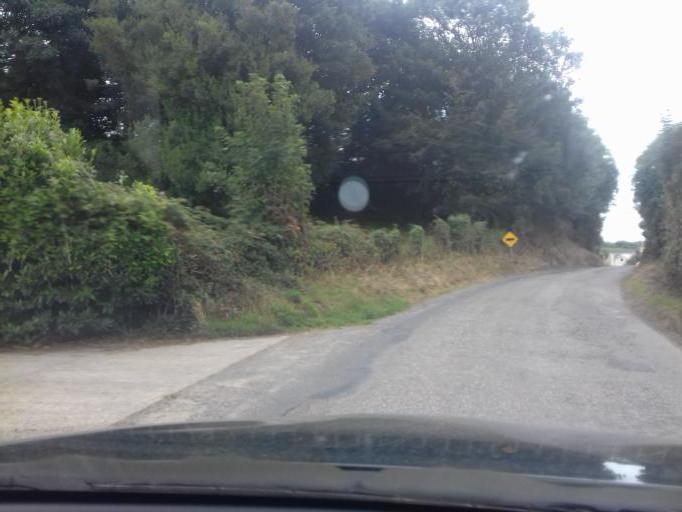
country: IE
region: Leinster
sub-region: Loch Garman
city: Castlebridge
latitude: 52.3946
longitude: -6.3940
